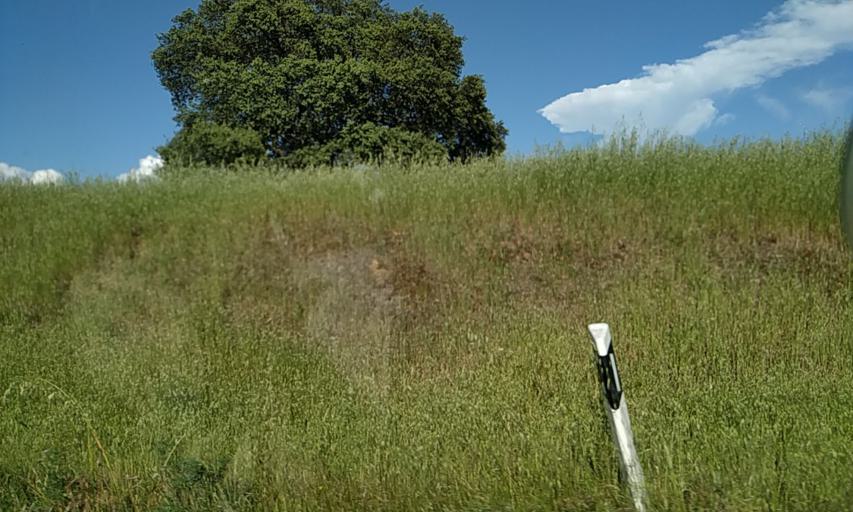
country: PT
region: Portalegre
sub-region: Portalegre
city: Urra
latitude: 39.0916
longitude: -7.4374
